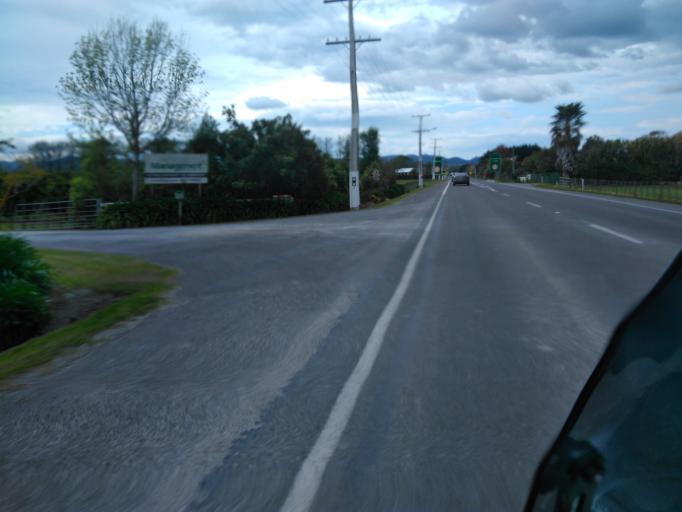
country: NZ
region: Gisborne
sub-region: Gisborne District
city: Gisborne
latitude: -38.6530
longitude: 177.9571
